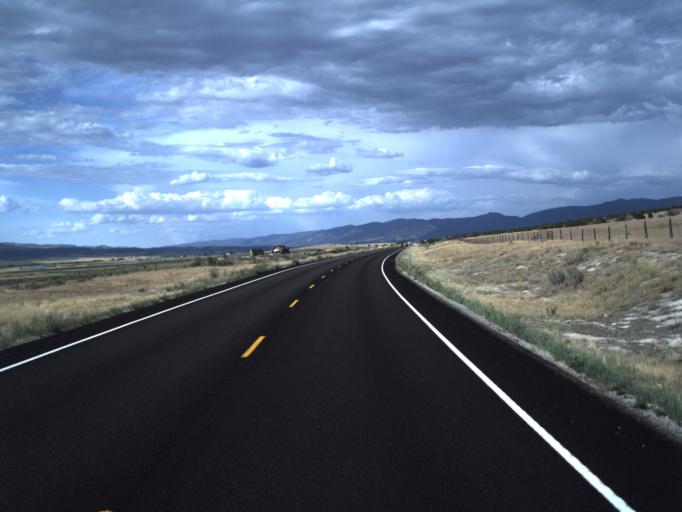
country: US
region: Utah
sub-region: Sanpete County
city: Moroni
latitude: 39.4545
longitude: -111.5418
